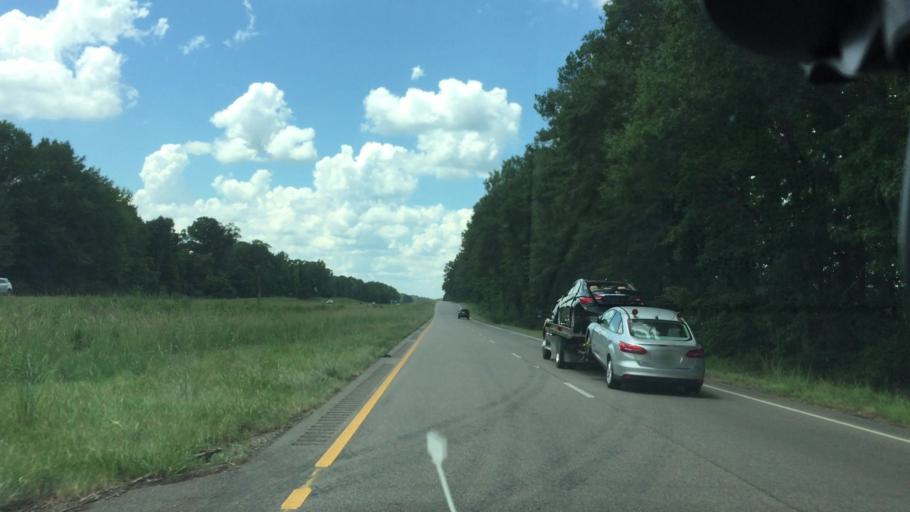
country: US
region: Alabama
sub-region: Montgomery County
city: Pike Road
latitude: 32.1383
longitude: -86.0926
